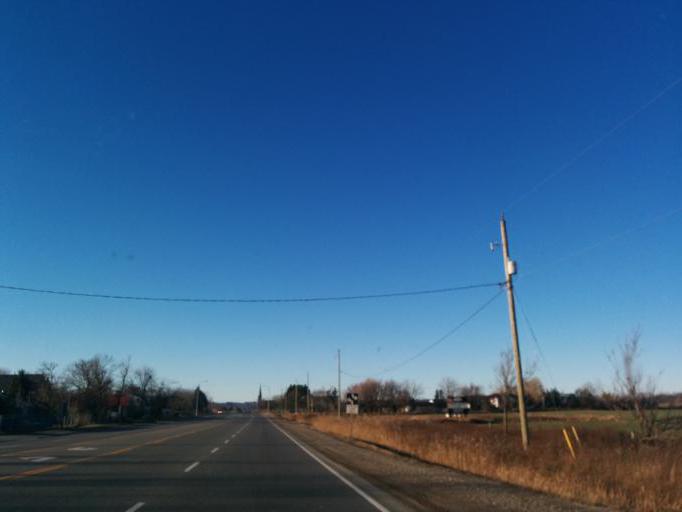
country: CA
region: Ontario
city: Brampton
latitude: 43.7918
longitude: -79.9028
